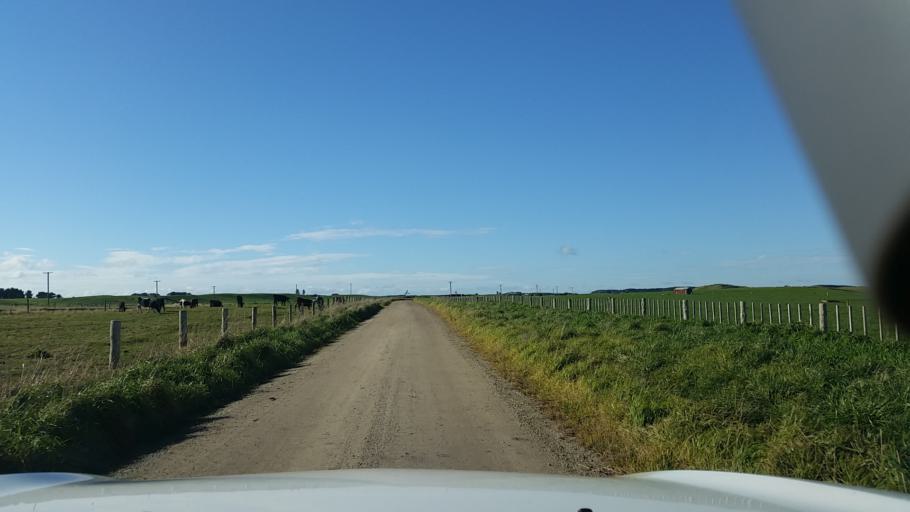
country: NZ
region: Taranaki
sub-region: South Taranaki District
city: Patea
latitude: -39.7744
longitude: 174.5493
